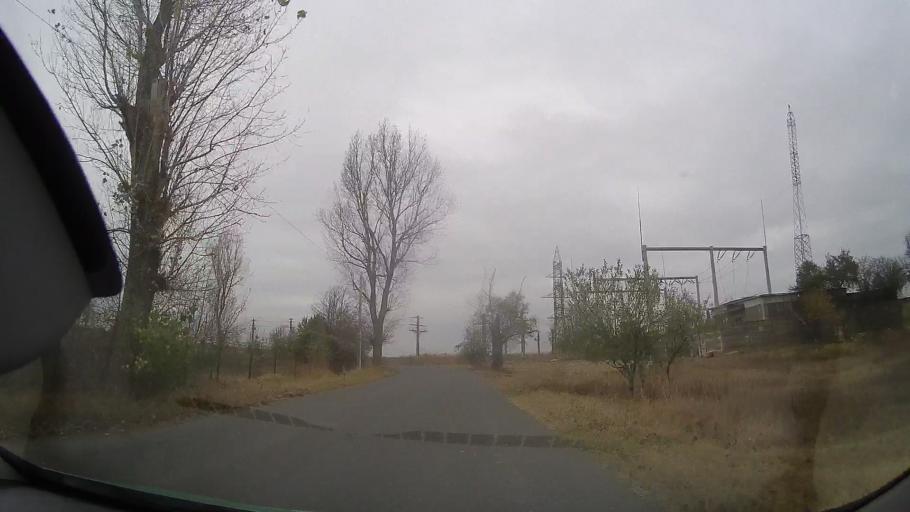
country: RO
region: Braila
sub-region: Comuna Rosiori
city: Rosiori
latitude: 44.8366
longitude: 27.3259
